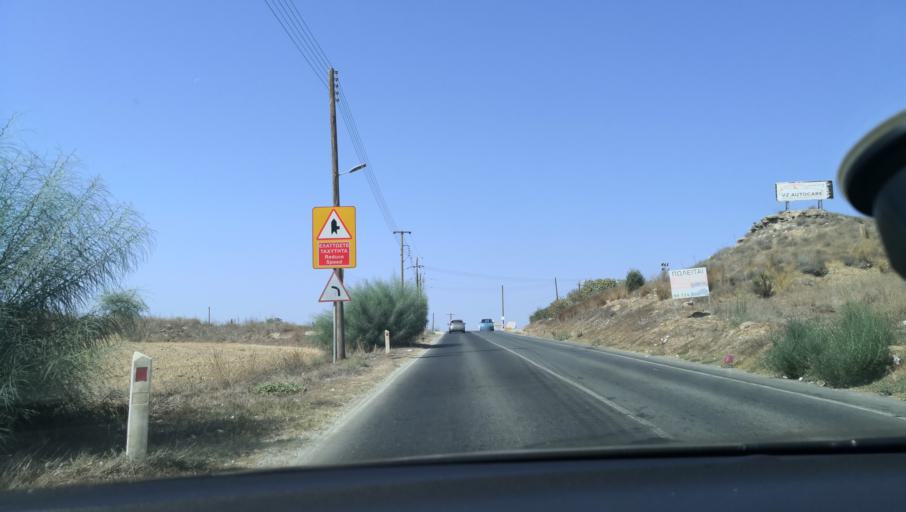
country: CY
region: Lefkosia
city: Kato Deftera
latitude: 35.1169
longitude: 33.2798
